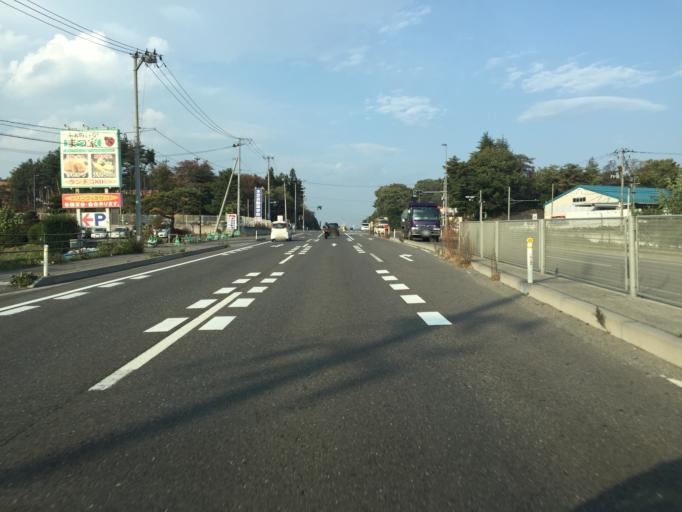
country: JP
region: Fukushima
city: Motomiya
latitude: 37.5486
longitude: 140.3998
